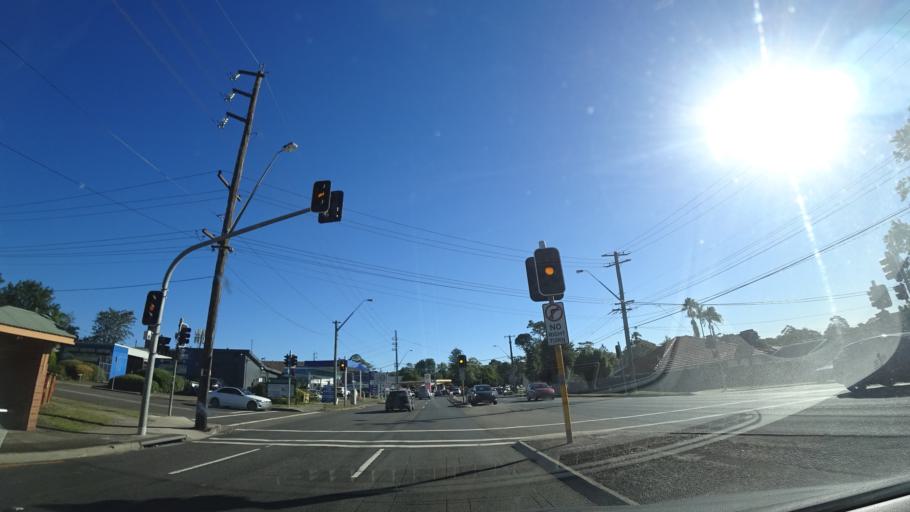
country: AU
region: New South Wales
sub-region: Warringah
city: Forestville
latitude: -33.7591
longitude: 151.2192
